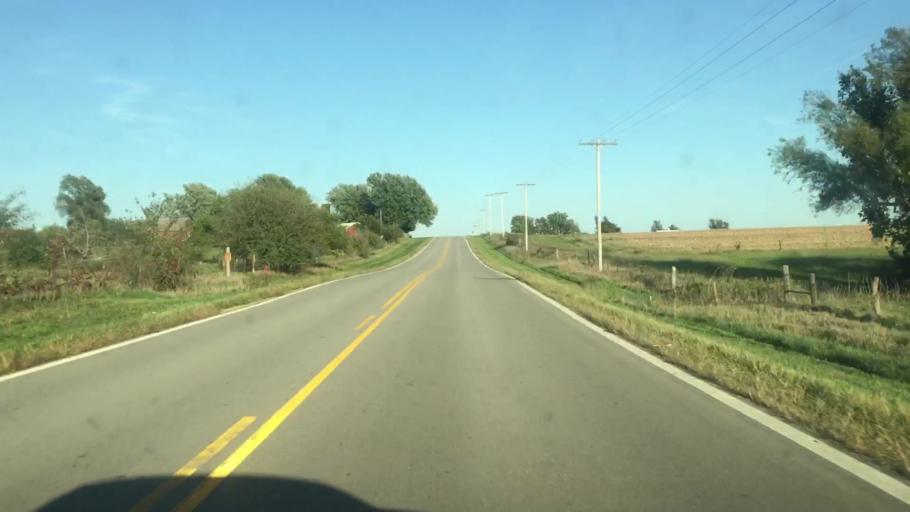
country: US
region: Kansas
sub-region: Brown County
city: Horton
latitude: 39.5876
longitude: -95.5876
